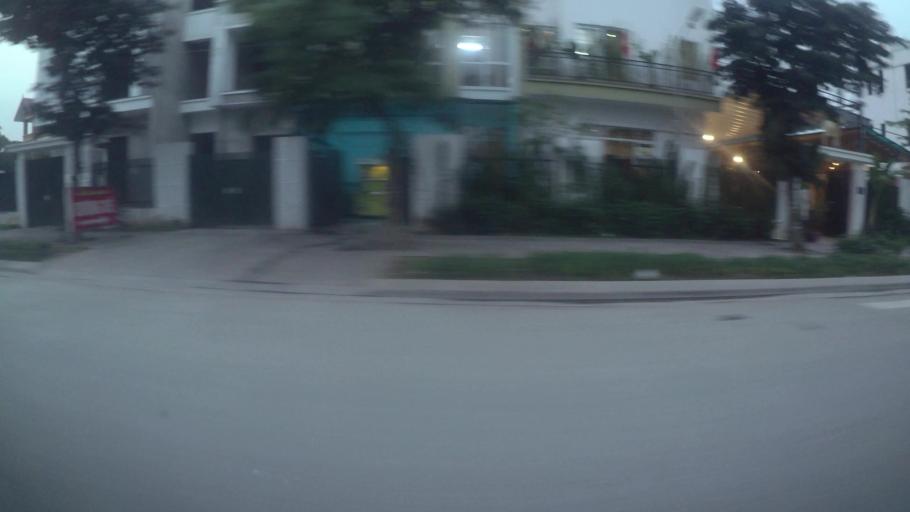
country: VN
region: Ha Noi
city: Tay Ho
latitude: 21.0655
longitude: 105.7910
